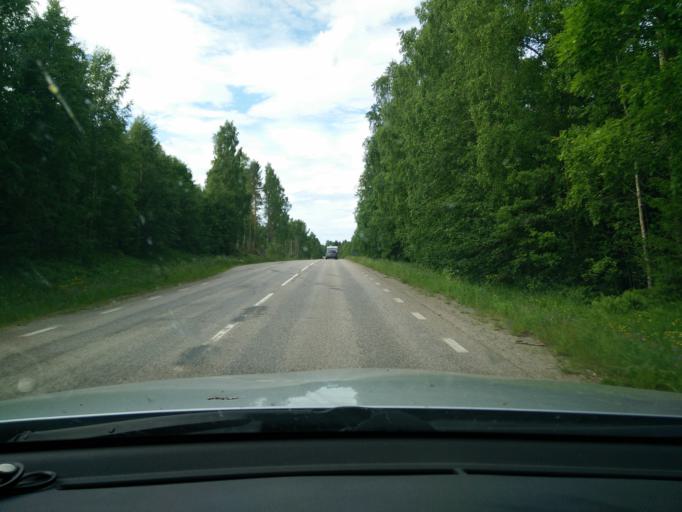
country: SE
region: Gaevleborg
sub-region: Nordanstigs Kommun
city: Bergsjoe
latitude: 61.9611
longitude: 17.0620
